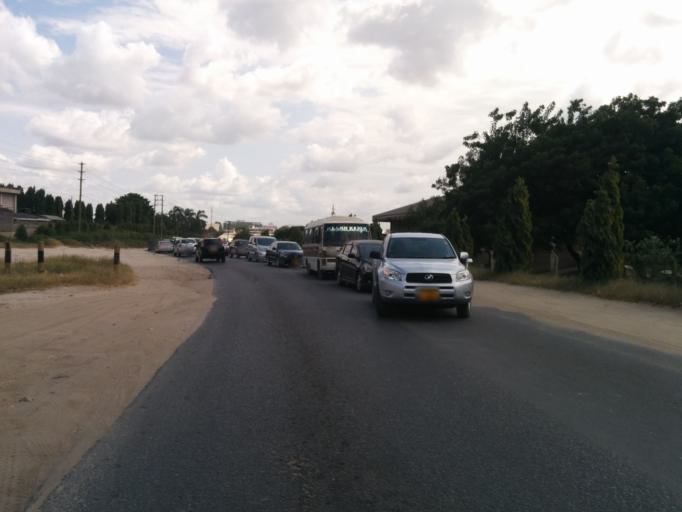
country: TZ
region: Dar es Salaam
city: Dar es Salaam
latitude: -6.8307
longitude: 39.2841
